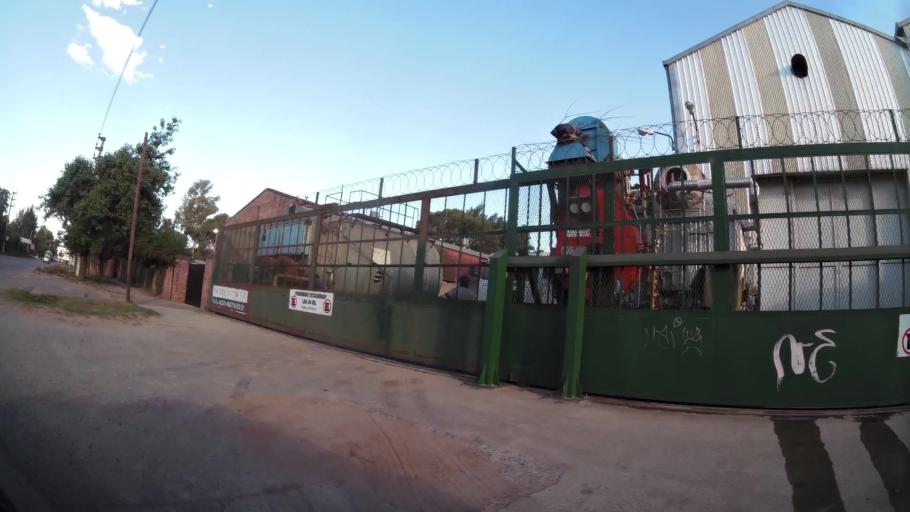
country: AR
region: Buenos Aires
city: Santa Catalina - Dique Lujan
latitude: -34.4659
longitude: -58.7485
